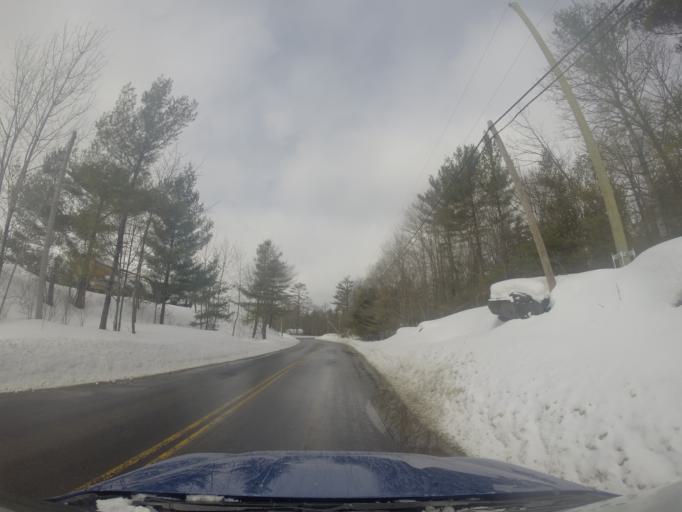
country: CA
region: Ontario
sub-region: Parry Sound District
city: Parry Sound
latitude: 45.3782
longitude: -80.0256
